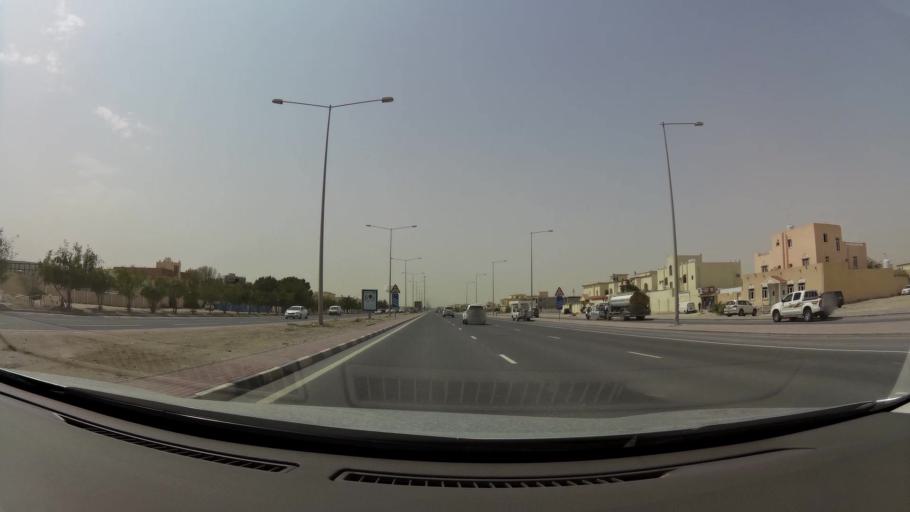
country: QA
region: Baladiyat ar Rayyan
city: Ar Rayyan
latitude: 25.2479
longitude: 51.4233
